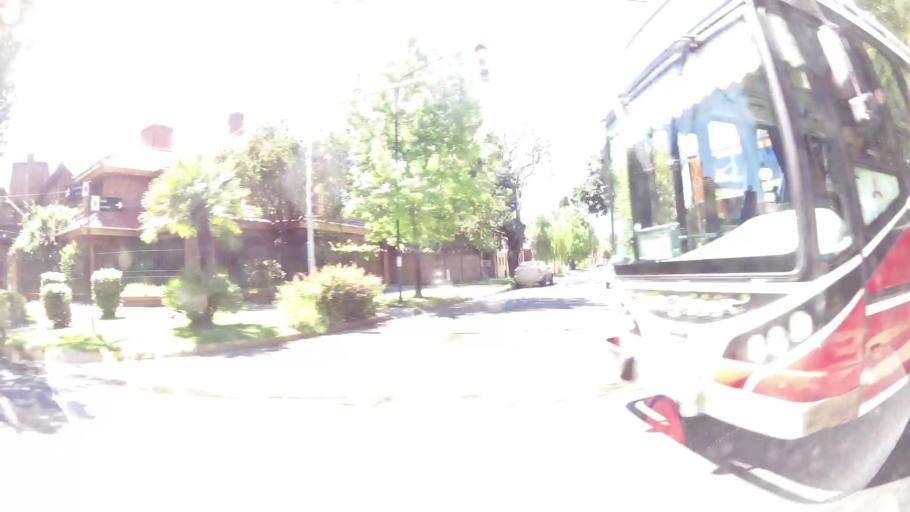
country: AR
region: Buenos Aires
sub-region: Partido de General San Martin
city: General San Martin
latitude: -34.5171
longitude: -58.5431
